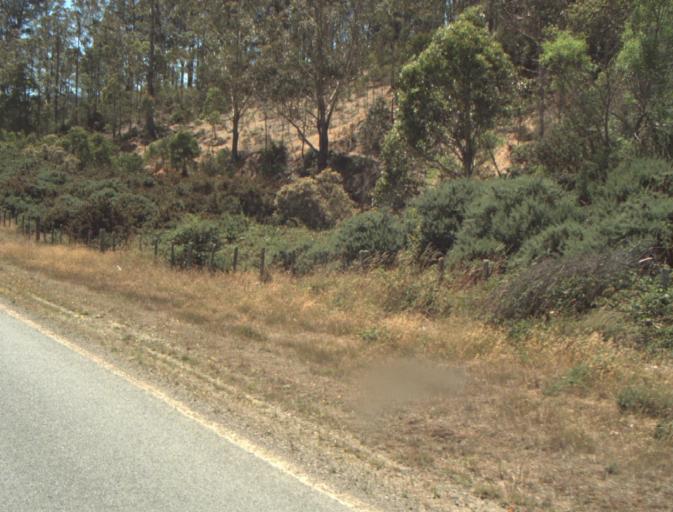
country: AU
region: Tasmania
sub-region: Dorset
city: Scottsdale
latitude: -41.2882
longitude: 147.3844
